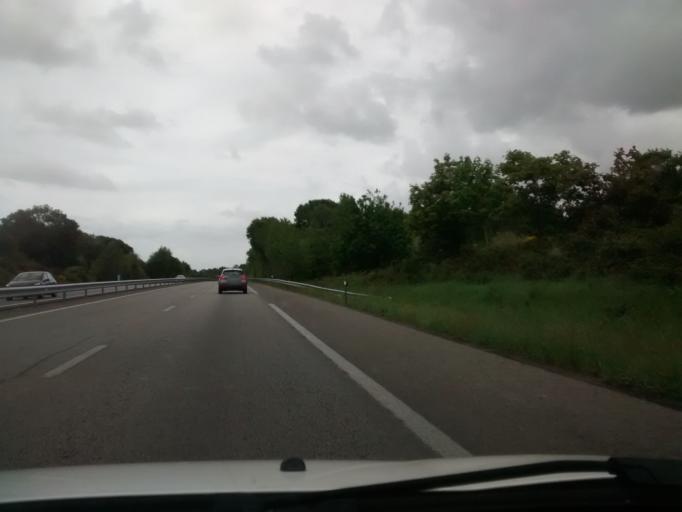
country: FR
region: Brittany
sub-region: Departement du Morbihan
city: Augan
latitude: 47.9283
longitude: -2.2436
